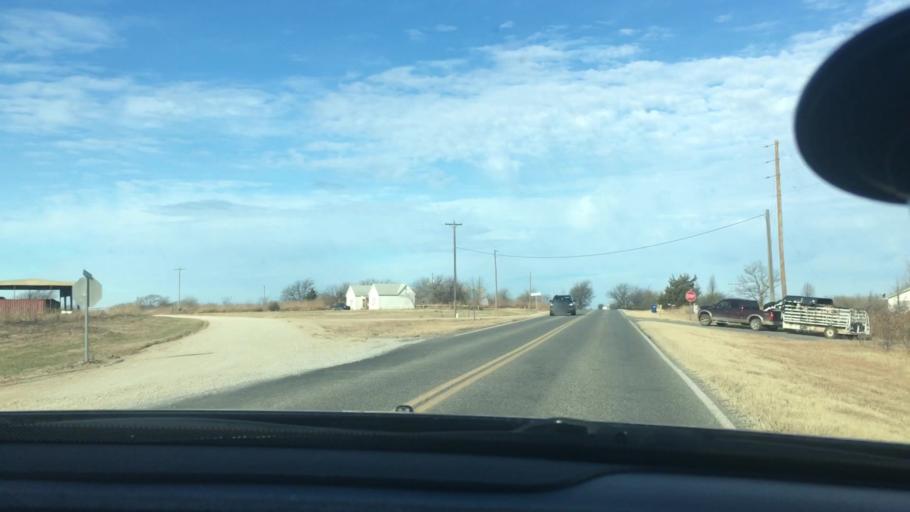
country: US
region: Oklahoma
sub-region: Seminole County
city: Konawa
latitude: 34.9706
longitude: -96.7775
